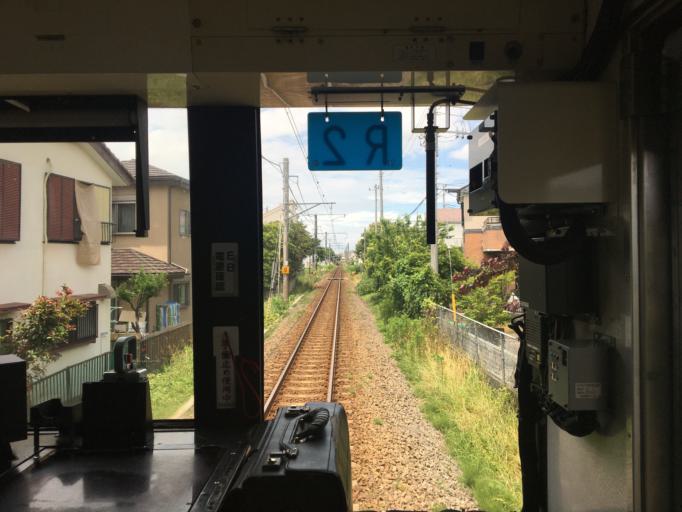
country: JP
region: Kanagawa
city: Chigasaki
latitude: 35.3537
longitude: 139.4005
